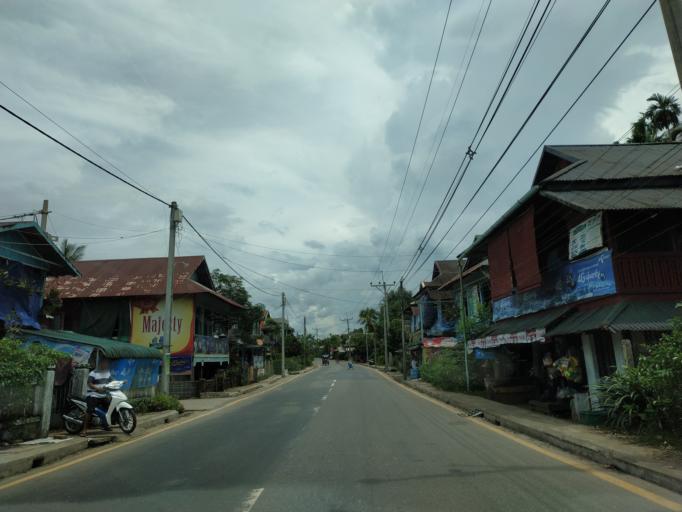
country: MM
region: Tanintharyi
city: Dawei
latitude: 14.0722
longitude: 98.2085
